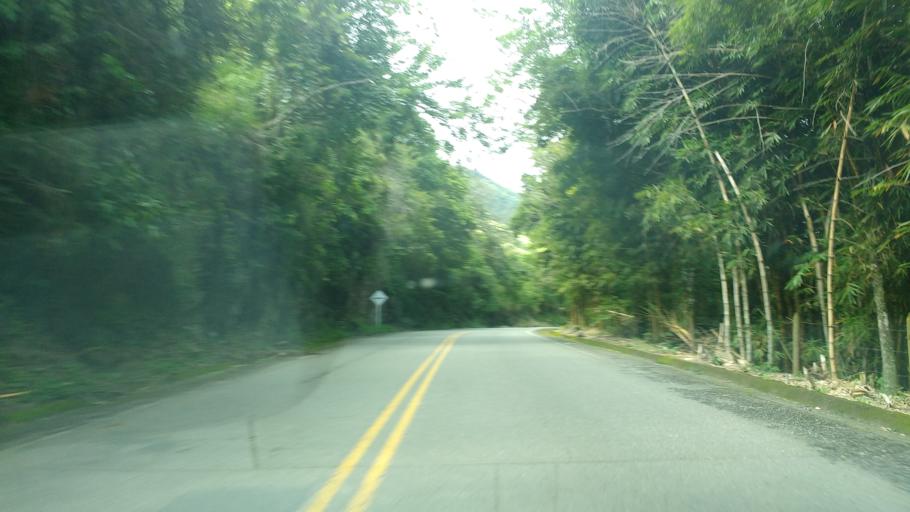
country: CO
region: Antioquia
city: Titiribi
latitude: 6.0310
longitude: -75.7625
